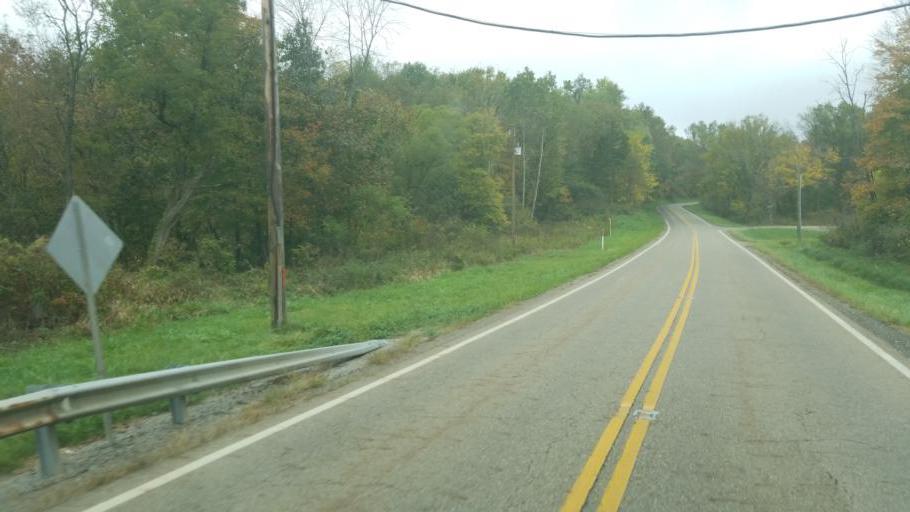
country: US
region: Ohio
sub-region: Carroll County
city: Lake Mohawk
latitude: 40.6112
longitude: -81.2755
